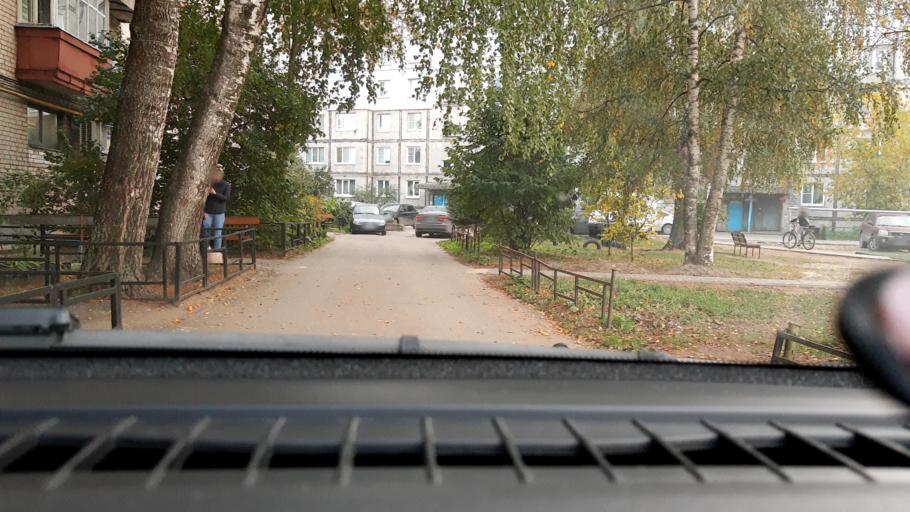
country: RU
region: Nizjnij Novgorod
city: Bor
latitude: 56.3651
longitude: 44.0574
